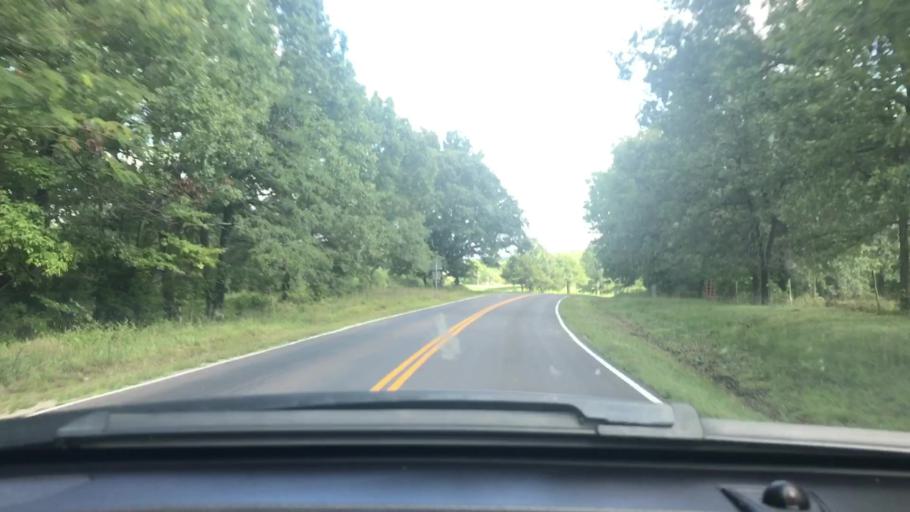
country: US
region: Missouri
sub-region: Wright County
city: Hartville
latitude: 37.3778
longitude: -92.3574
